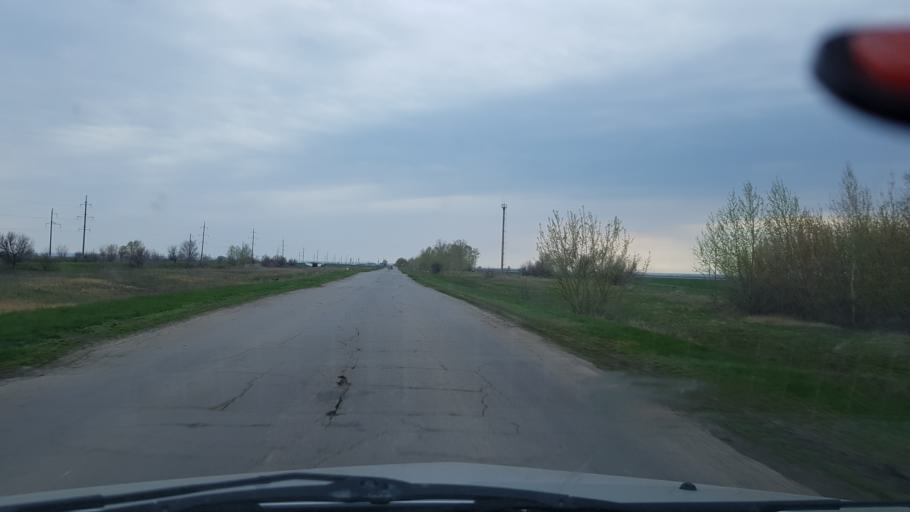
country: RU
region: Samara
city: Khryashchevka
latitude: 53.6688
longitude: 49.1325
